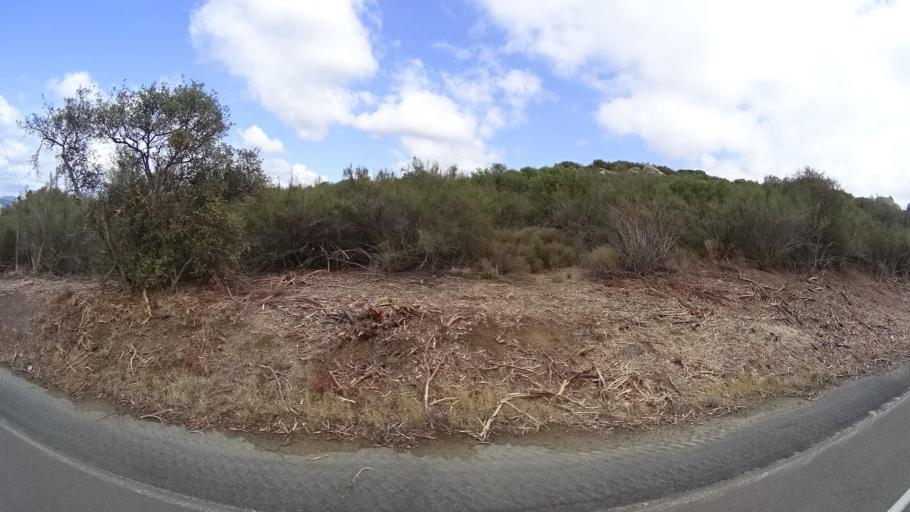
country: US
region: California
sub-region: San Diego County
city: Campo
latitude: 32.6750
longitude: -116.5059
